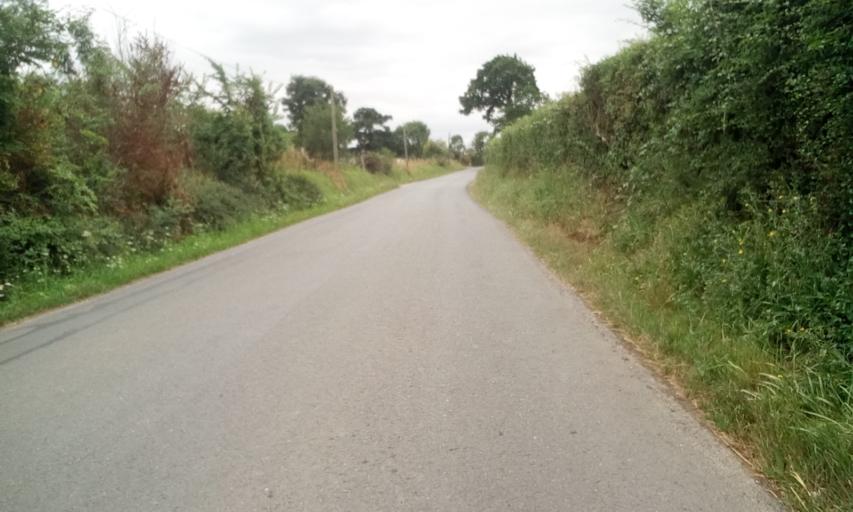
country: FR
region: Lower Normandy
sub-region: Departement du Calvados
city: Troarn
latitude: 49.1956
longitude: -0.1789
